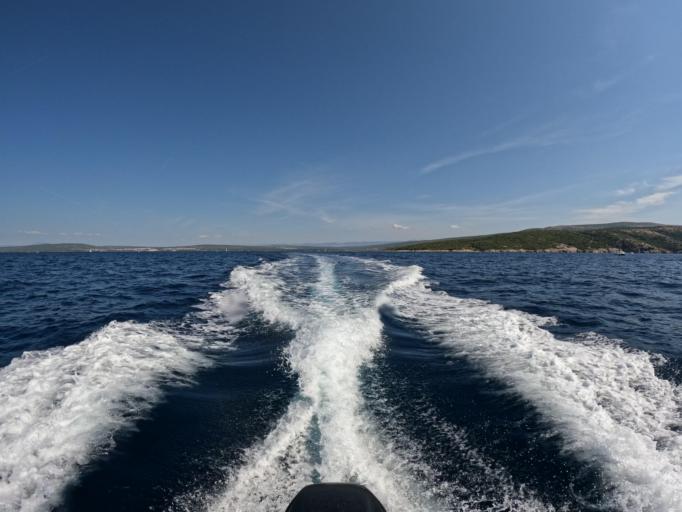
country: HR
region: Primorsko-Goranska
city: Punat
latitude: 44.9706
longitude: 14.6086
